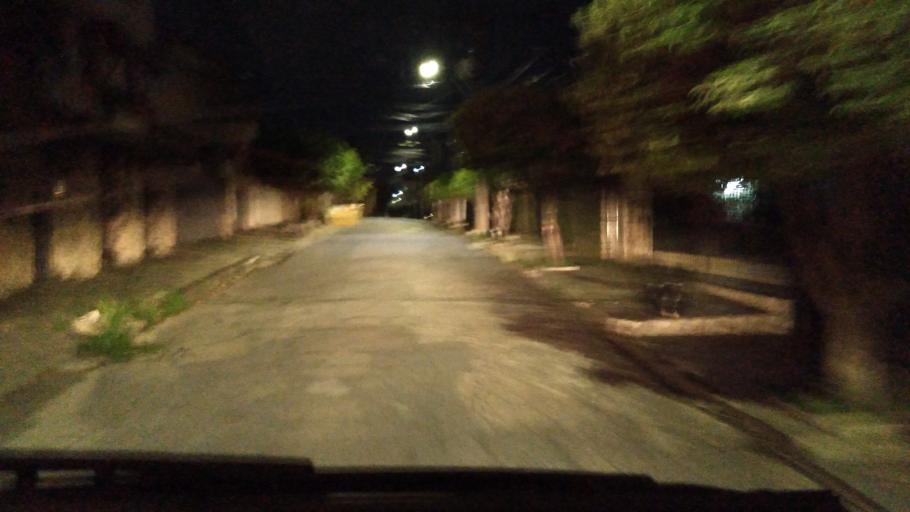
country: BR
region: Minas Gerais
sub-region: Belo Horizonte
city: Belo Horizonte
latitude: -19.8992
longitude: -43.9745
